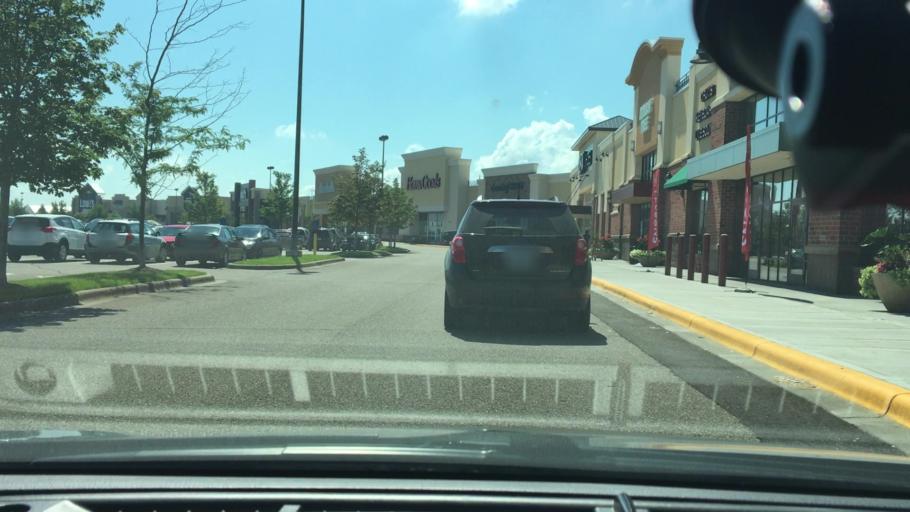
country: US
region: Minnesota
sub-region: Hennepin County
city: Maple Grove
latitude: 45.0912
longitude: -93.4273
